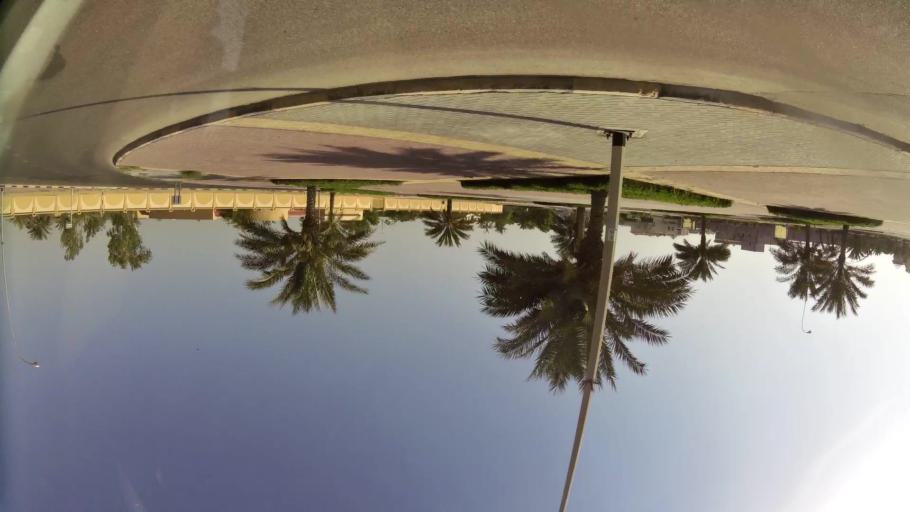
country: AE
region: Ajman
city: Ajman
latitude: 25.4119
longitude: 55.4676
